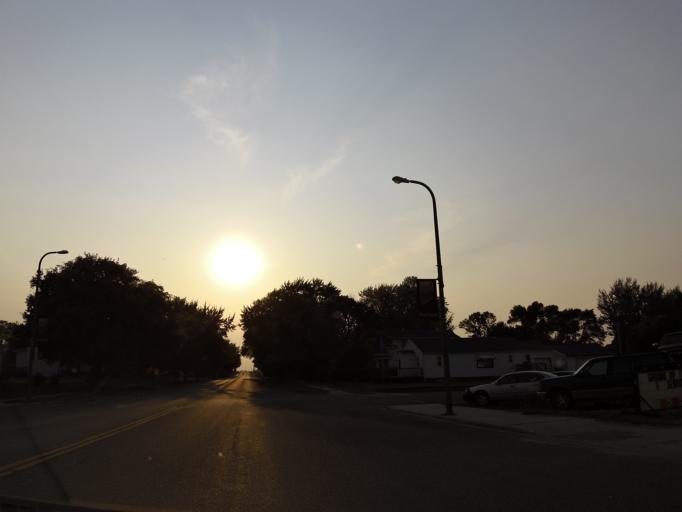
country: US
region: North Dakota
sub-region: Traill County
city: Mayville
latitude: 47.4985
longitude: -97.3720
